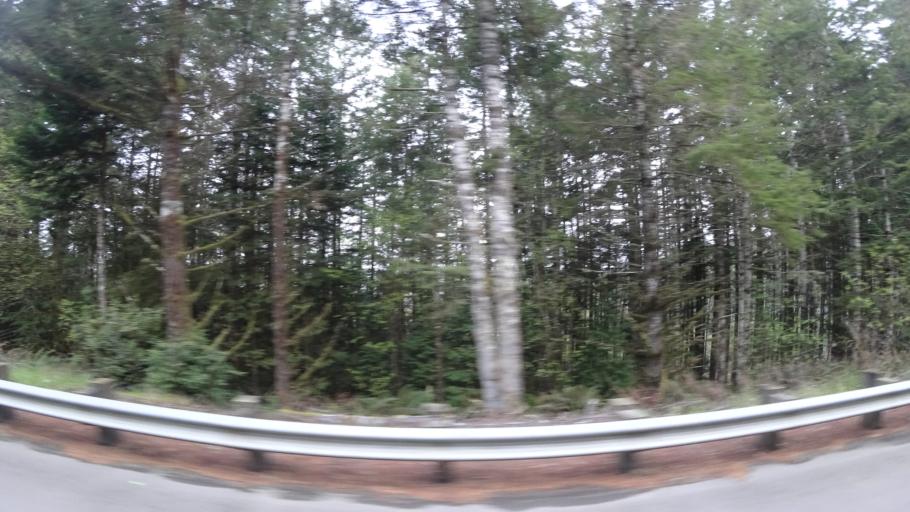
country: US
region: Oregon
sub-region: Coos County
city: Barview
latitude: 43.2479
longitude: -124.2870
